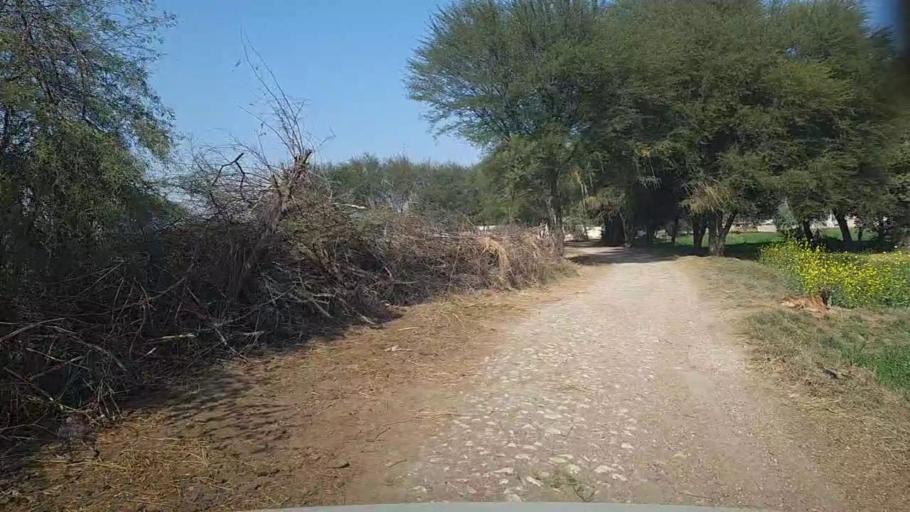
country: PK
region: Sindh
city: Khairpur
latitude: 28.0574
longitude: 69.6727
